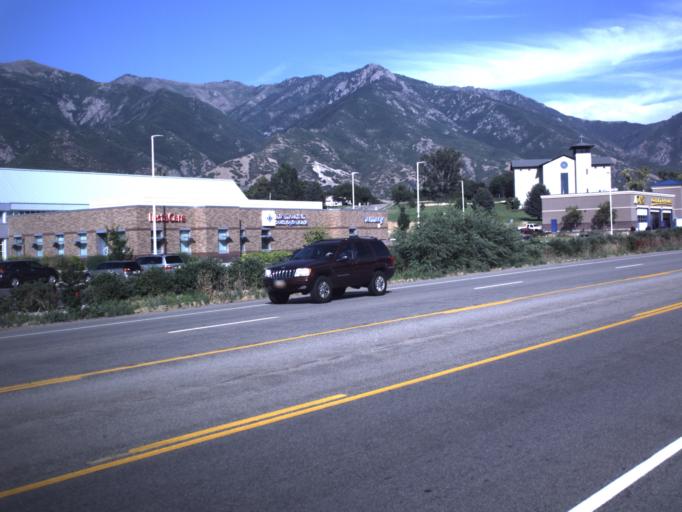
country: US
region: Utah
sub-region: Weber County
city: Washington Terrace
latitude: 41.1642
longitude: -111.9544
